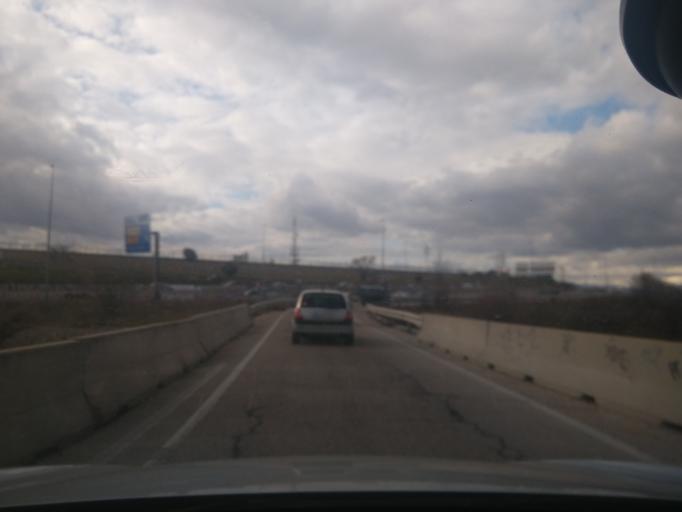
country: ES
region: Madrid
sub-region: Provincia de Madrid
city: Tres Cantos
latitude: 40.5497
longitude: -3.7043
